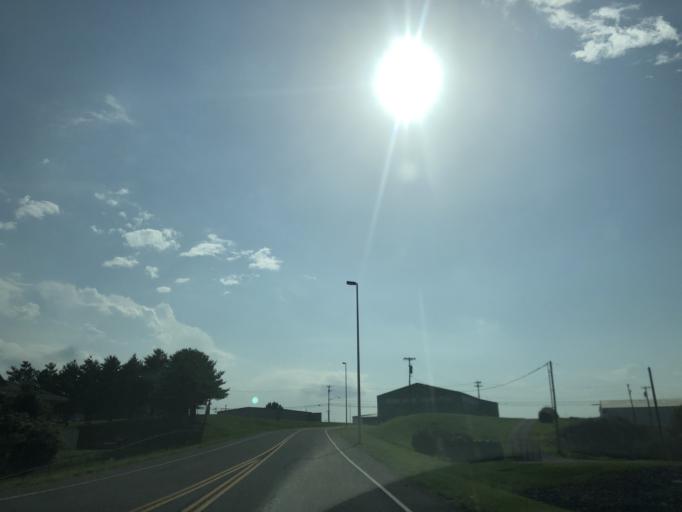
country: US
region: Tennessee
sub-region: Davidson County
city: Oak Hill
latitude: 36.1146
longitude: -86.6757
